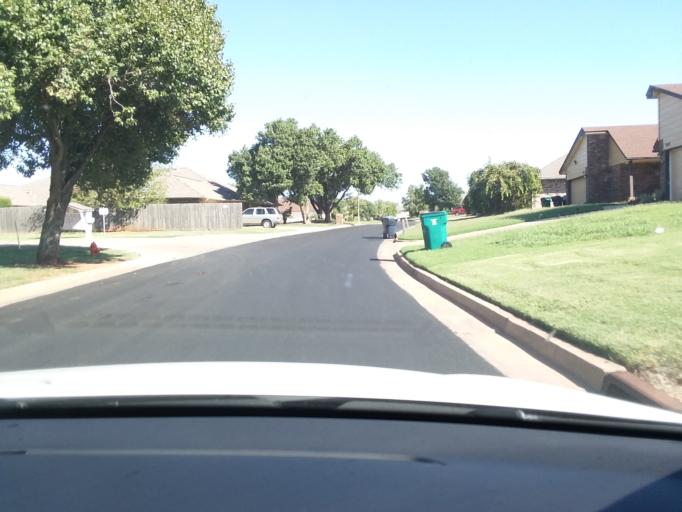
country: US
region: Oklahoma
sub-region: Oklahoma County
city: The Village
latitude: 35.5984
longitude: -97.5654
